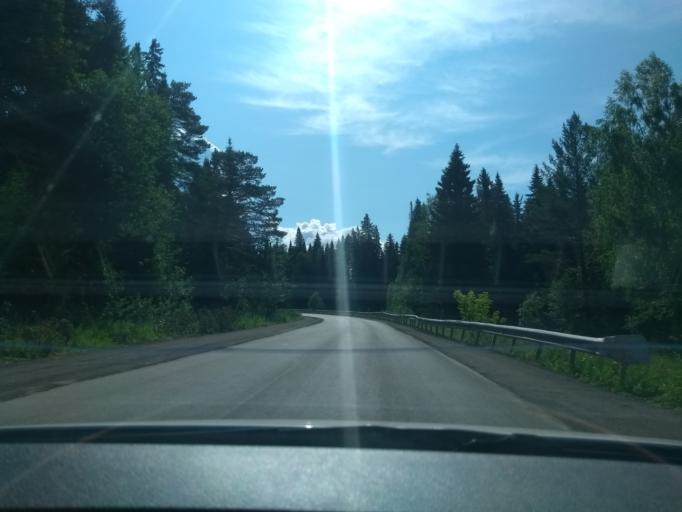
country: RU
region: Perm
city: Bershet'
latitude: 57.8177
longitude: 56.5281
